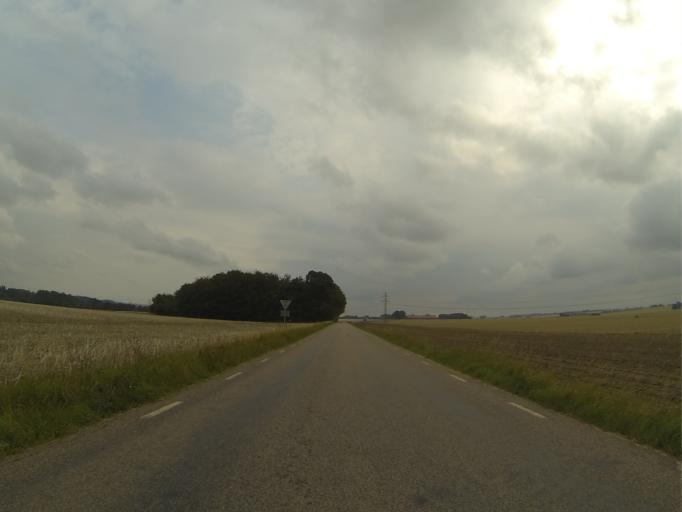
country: SE
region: Skane
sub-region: Lunds Kommun
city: Lund
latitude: 55.7732
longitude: 13.2314
